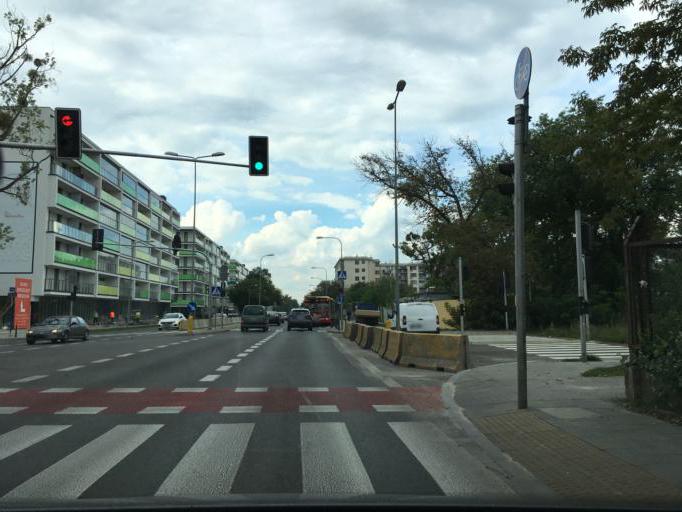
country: PL
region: Masovian Voivodeship
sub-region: Warszawa
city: Zoliborz
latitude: 52.2567
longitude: 20.9678
